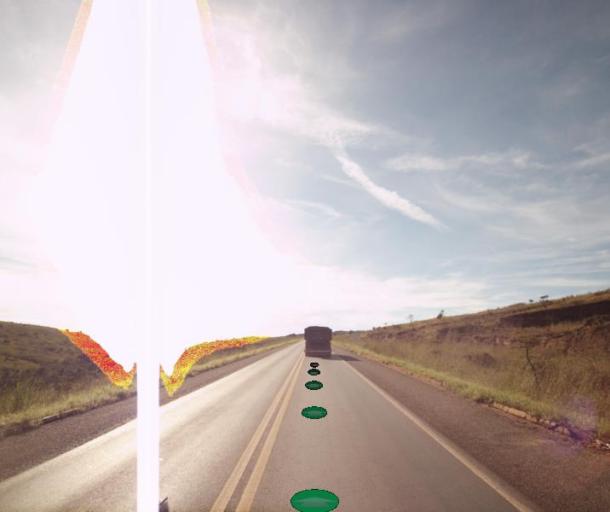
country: BR
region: Federal District
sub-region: Brasilia
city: Brasilia
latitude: -15.7548
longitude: -48.3419
